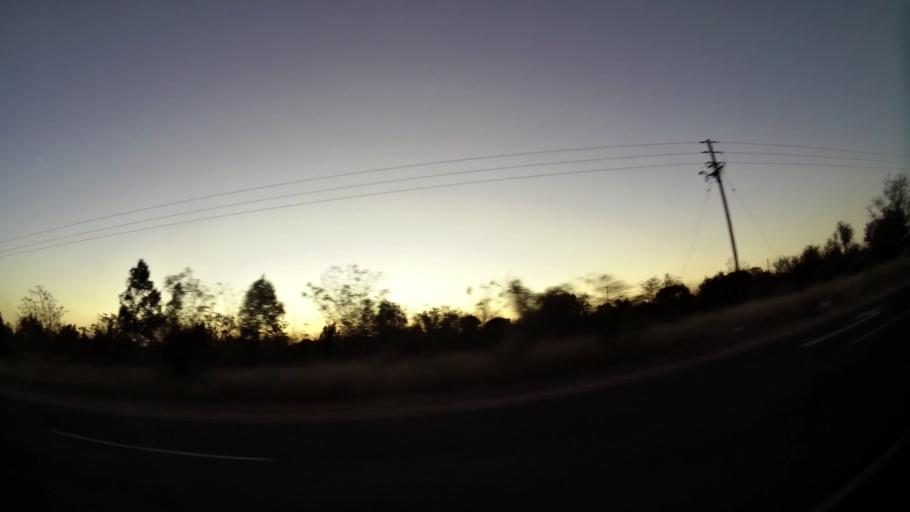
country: ZA
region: North-West
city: Ga-Rankuwa
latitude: -25.6380
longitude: 27.9517
